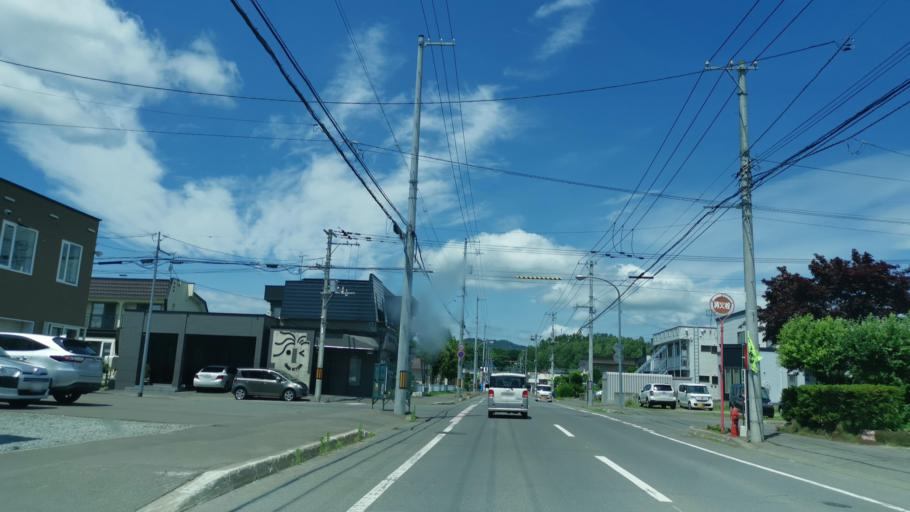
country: JP
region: Hokkaido
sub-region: Asahikawa-shi
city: Asahikawa
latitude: 43.7943
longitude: 142.3327
